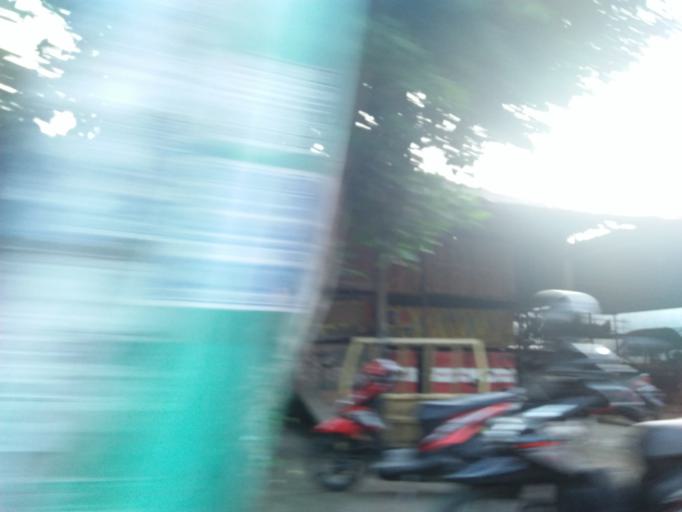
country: ID
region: Daerah Istimewa Yogyakarta
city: Sewon
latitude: -7.8547
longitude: 110.4097
